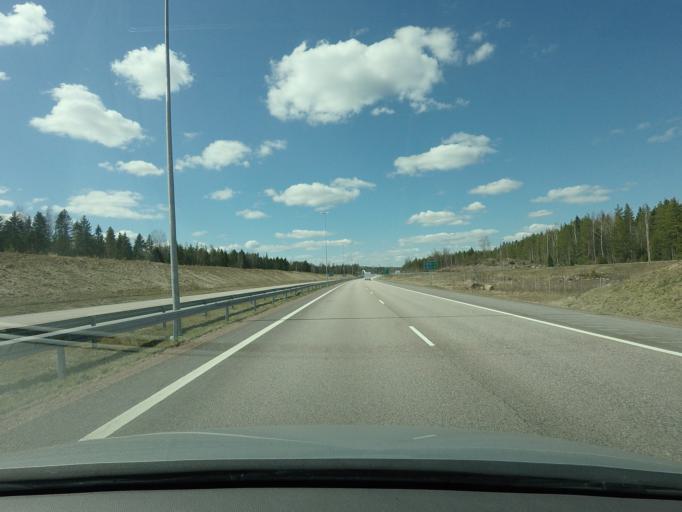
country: FI
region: Uusimaa
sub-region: Loviisa
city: Ruotsinpyhtaeae
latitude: 60.4879
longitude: 26.4732
